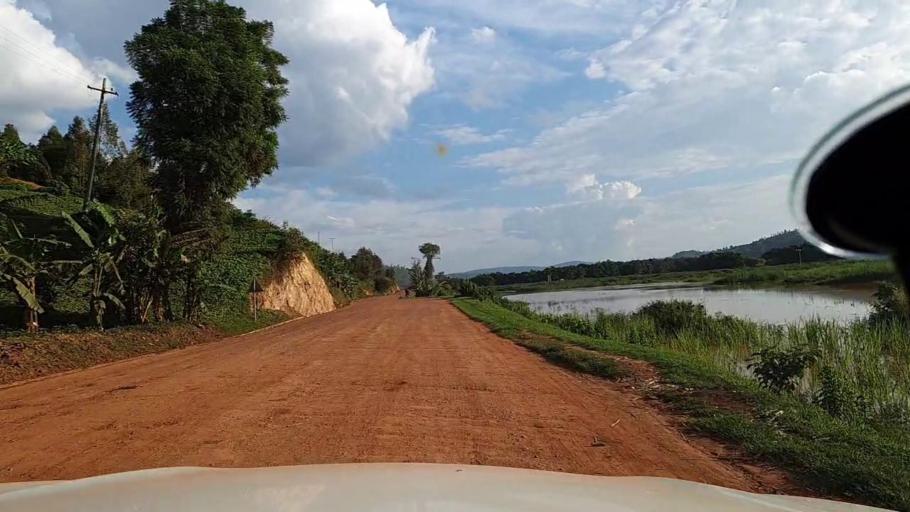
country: RW
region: Kigali
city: Kigali
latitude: -1.9344
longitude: 29.9973
